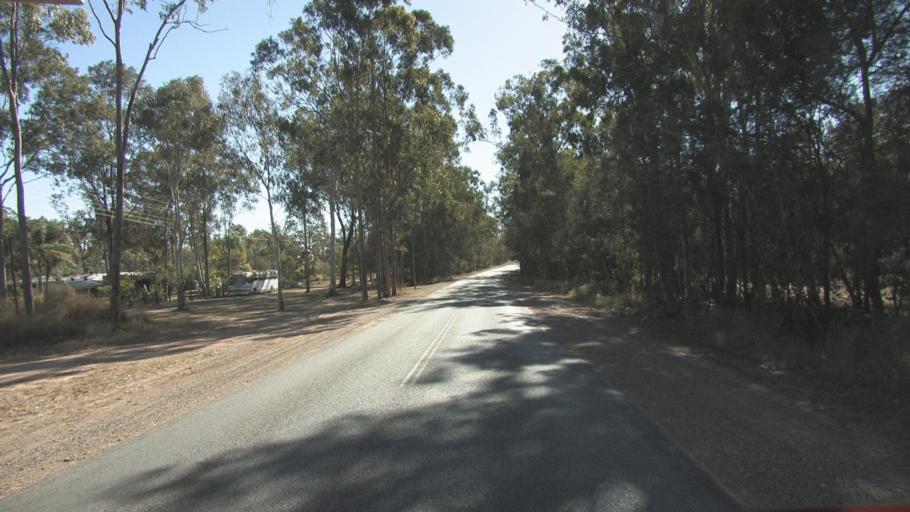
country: AU
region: Queensland
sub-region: Logan
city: North Maclean
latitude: -27.7487
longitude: 152.9923
